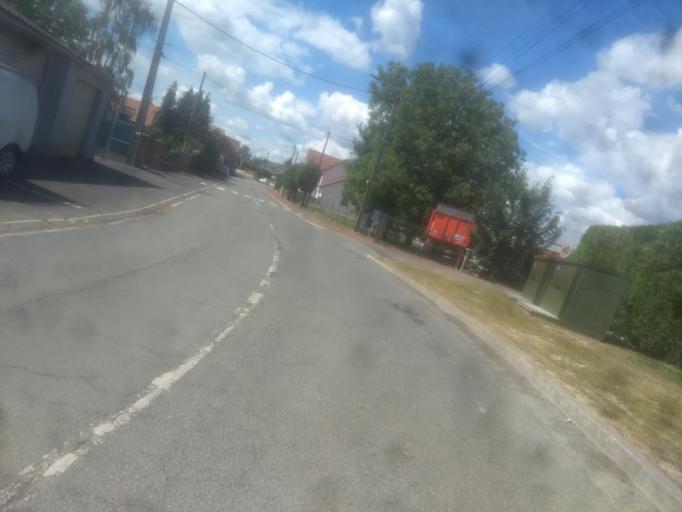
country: FR
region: Nord-Pas-de-Calais
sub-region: Departement du Pas-de-Calais
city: Croisilles
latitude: 50.2298
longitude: 2.8414
